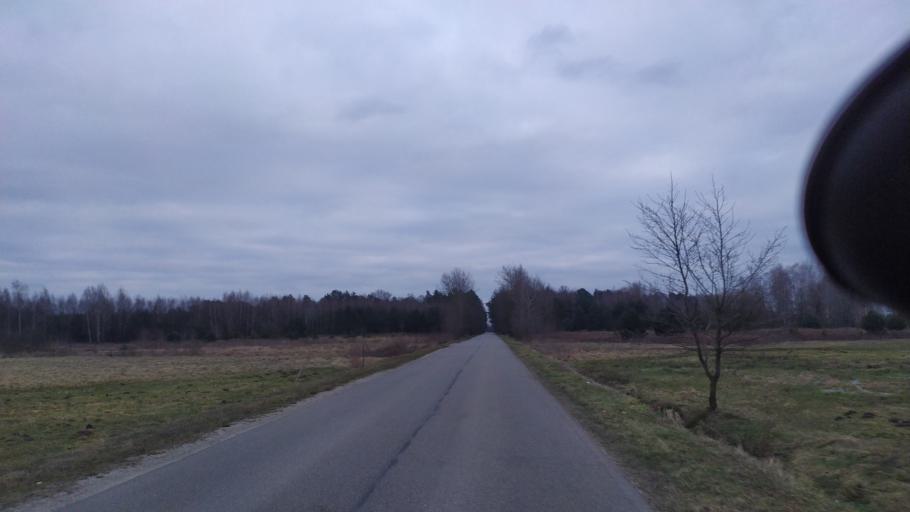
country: PL
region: Lublin Voivodeship
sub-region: Powiat lubartowski
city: Abramow
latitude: 51.4235
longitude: 22.3166
